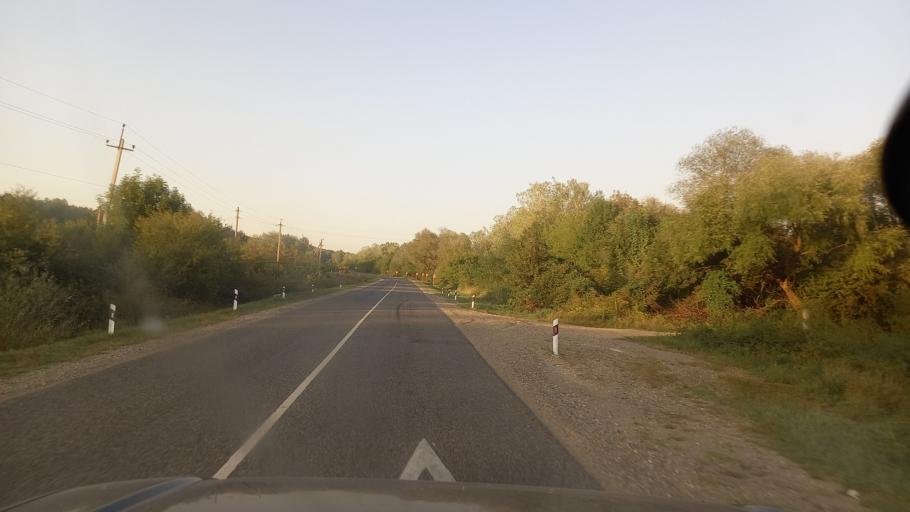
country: RU
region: Krasnodarskiy
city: Smolenskaya
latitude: 44.7562
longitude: 38.7661
